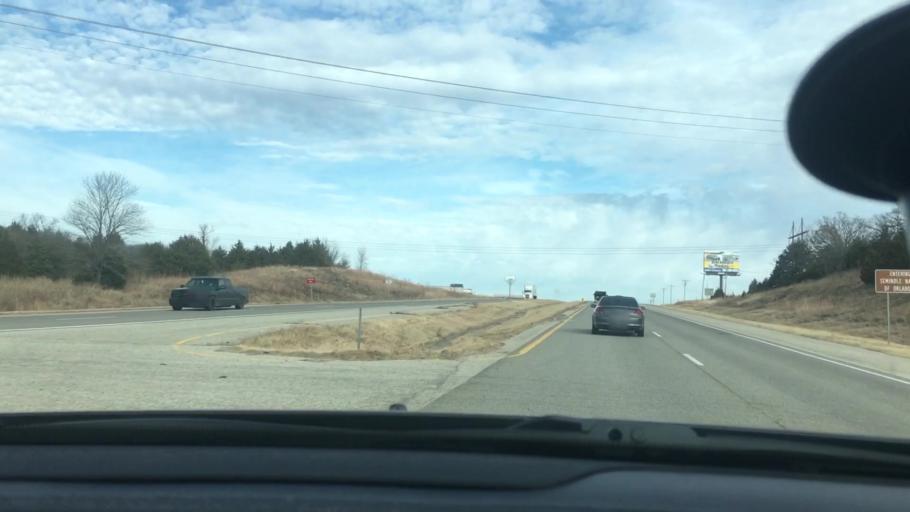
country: US
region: Oklahoma
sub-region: Seminole County
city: Konawa
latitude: 34.9354
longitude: -96.6832
